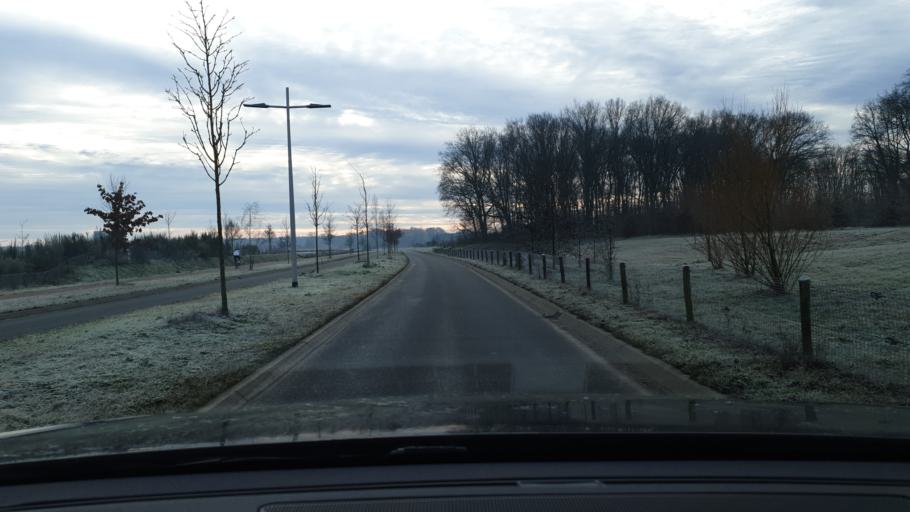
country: NL
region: North Brabant
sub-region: Gemeente Veldhoven
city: Oerle
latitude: 51.4242
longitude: 5.3572
